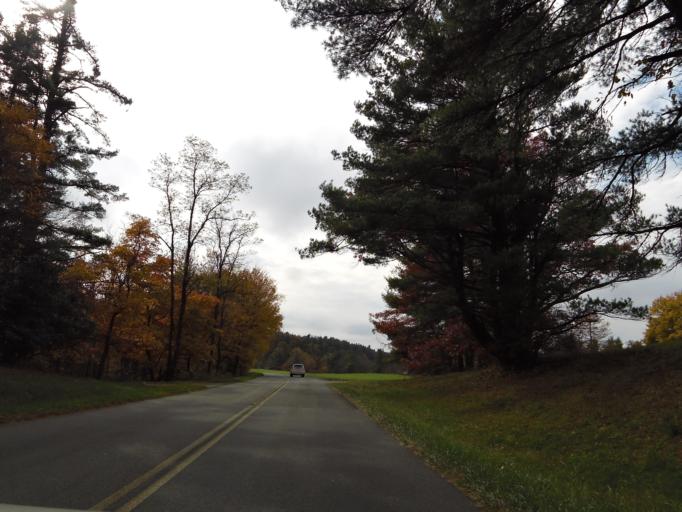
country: US
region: Virginia
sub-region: Carroll County
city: Cana
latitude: 36.6260
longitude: -80.7487
